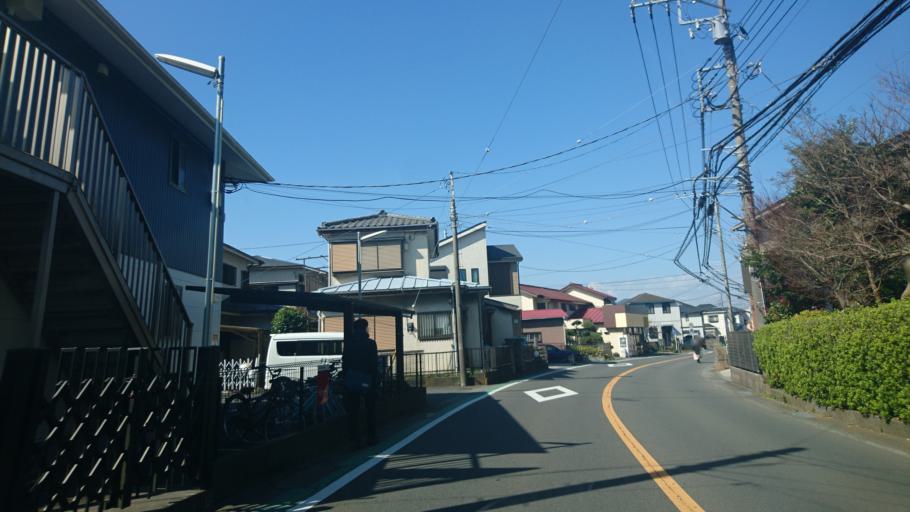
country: JP
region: Kanagawa
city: Fujisawa
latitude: 35.3864
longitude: 139.4764
